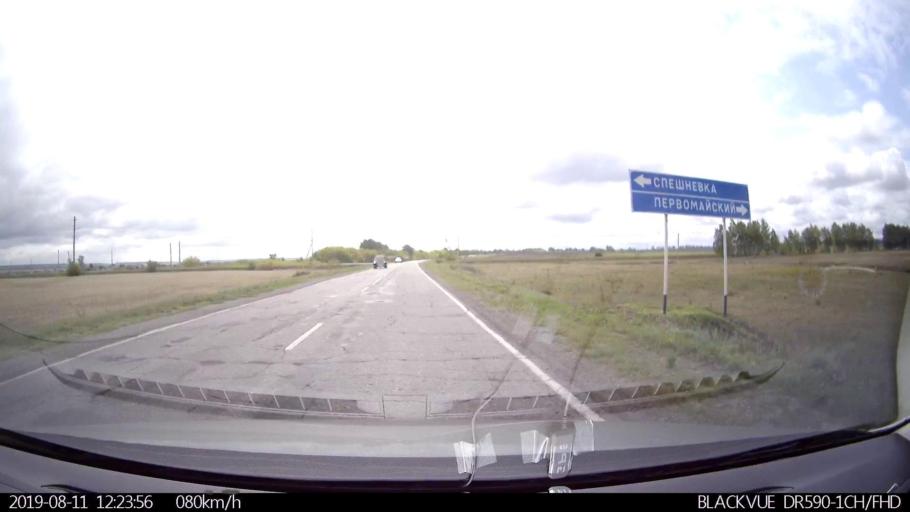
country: RU
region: Ulyanovsk
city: Ignatovka
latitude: 53.8893
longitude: 47.9502
